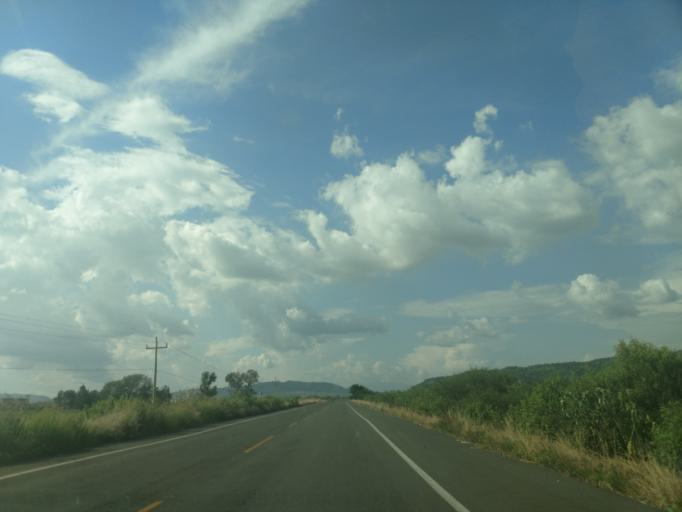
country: MX
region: Jalisco
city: Antonio Escobedo
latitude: 20.8960
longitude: -103.9941
